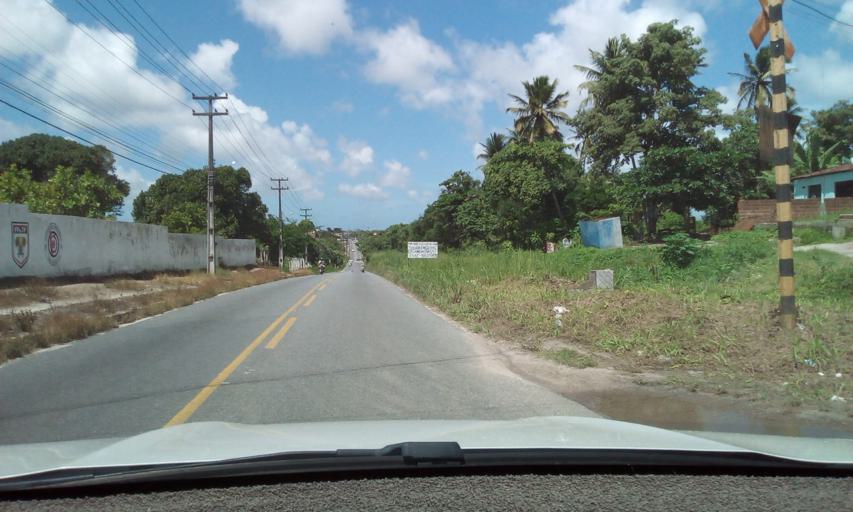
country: BR
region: Paraiba
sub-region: Bayeux
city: Bayeux
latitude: -7.1226
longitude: -34.9355
